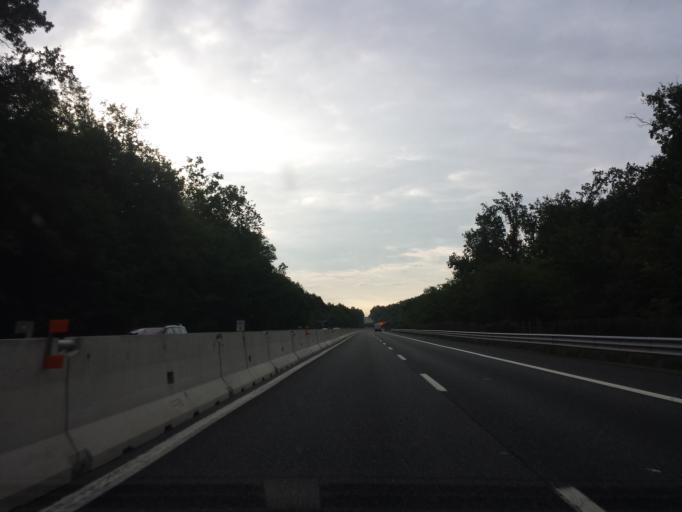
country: IT
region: Lombardy
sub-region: Provincia di Varese
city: Vergiate
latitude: 45.7162
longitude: 8.7068
